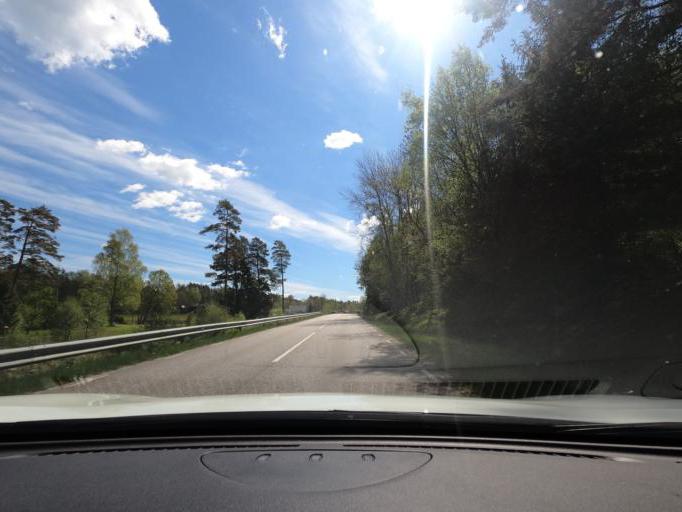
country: SE
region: Halland
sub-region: Kungsbacka Kommun
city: Fjaeras kyrkby
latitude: 57.4098
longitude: 12.2189
